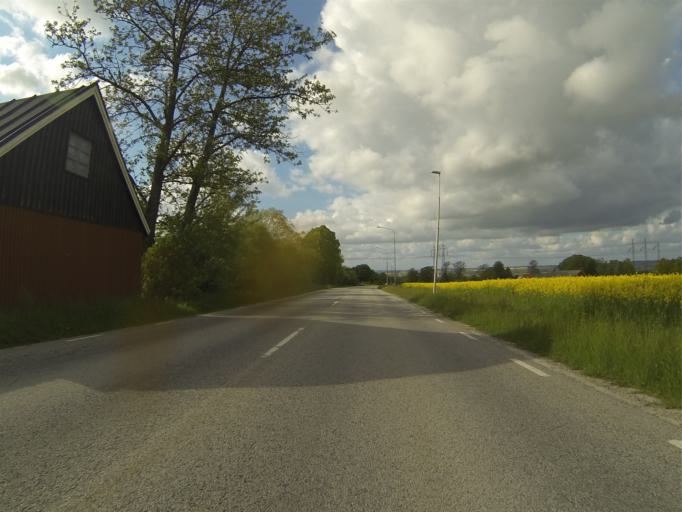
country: SE
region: Skane
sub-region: Lunds Kommun
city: Genarp
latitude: 55.7065
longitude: 13.3435
